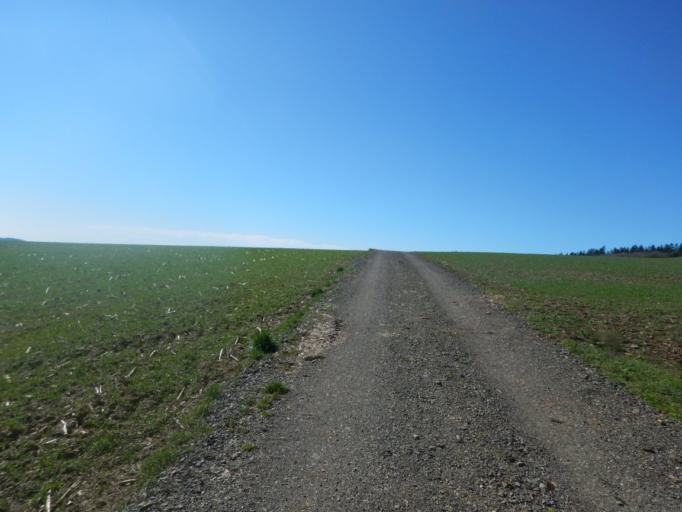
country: LU
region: Diekirch
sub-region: Canton de Wiltz
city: Eschweiler
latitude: 49.9971
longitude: 5.9257
